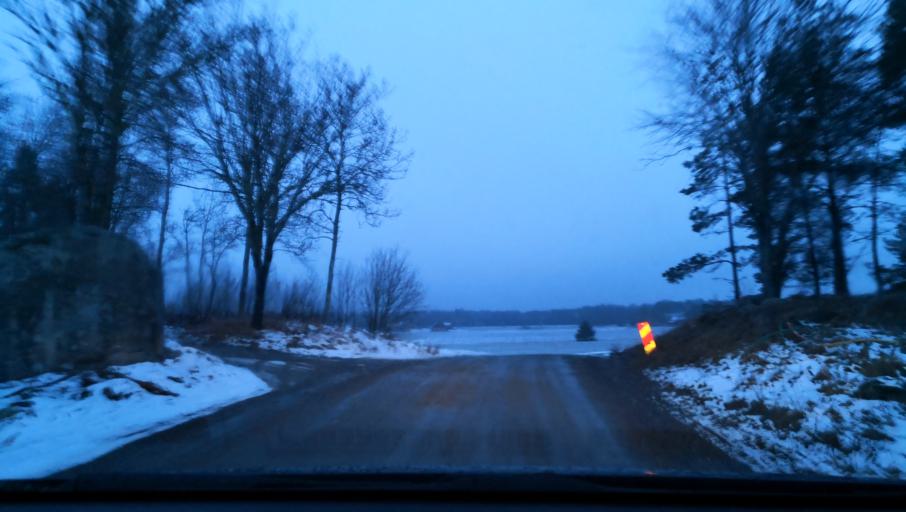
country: SE
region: Soedermanland
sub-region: Eskilstuna Kommun
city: Kvicksund
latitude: 59.3759
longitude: 16.2993
